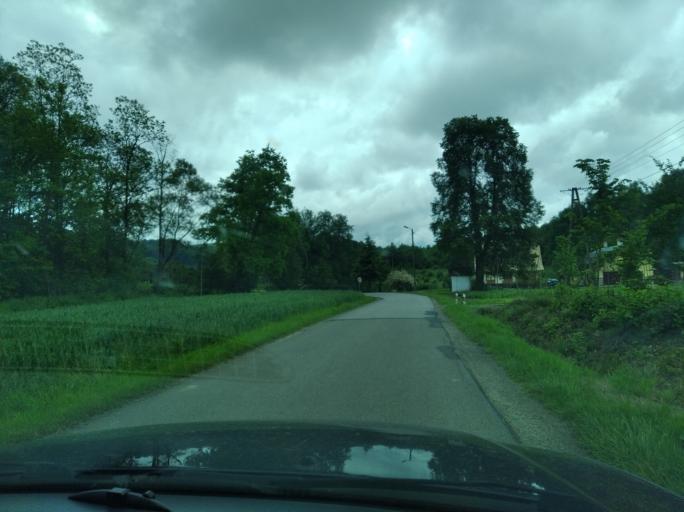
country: PL
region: Subcarpathian Voivodeship
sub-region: Powiat przemyski
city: Nienadowa
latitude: 49.8475
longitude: 22.4114
